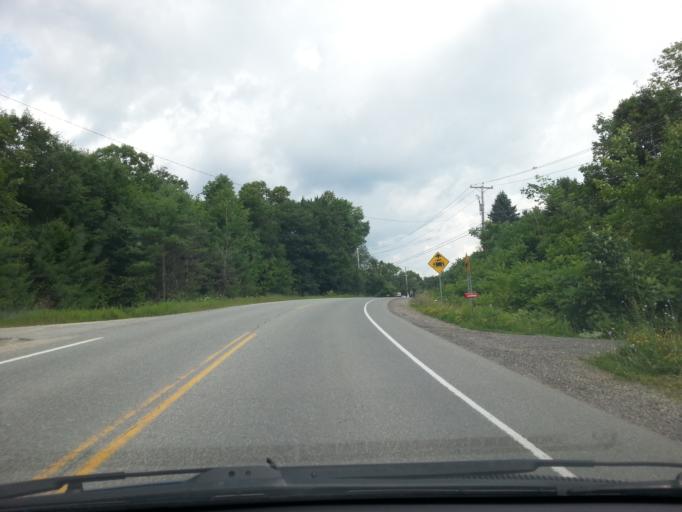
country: CA
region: Quebec
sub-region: Outaouais
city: Val-des-Monts
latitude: 45.6206
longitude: -75.6321
